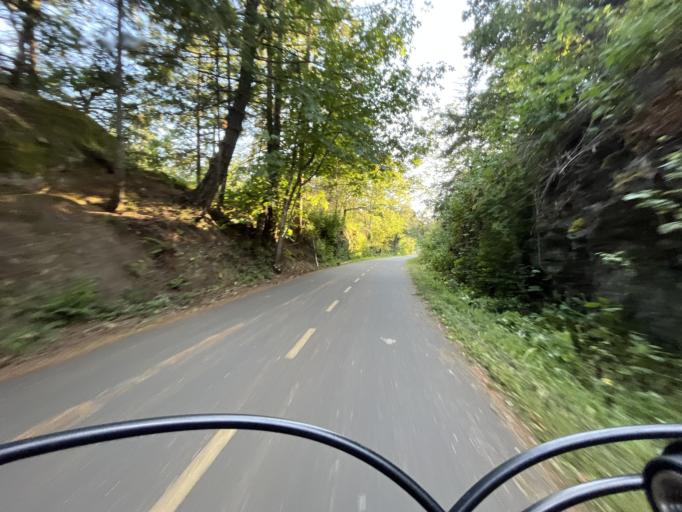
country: CA
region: British Columbia
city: Colwood
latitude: 48.4488
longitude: -123.4705
